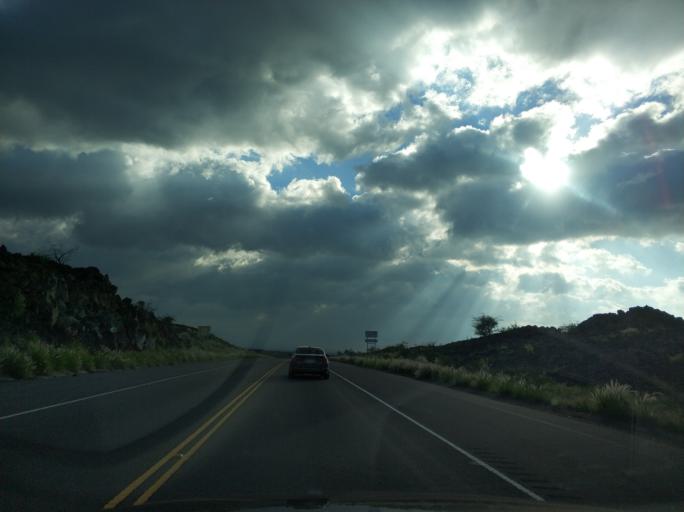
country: US
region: Hawaii
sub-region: Hawaii County
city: Waikoloa Village
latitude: 19.9413
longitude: -155.8370
